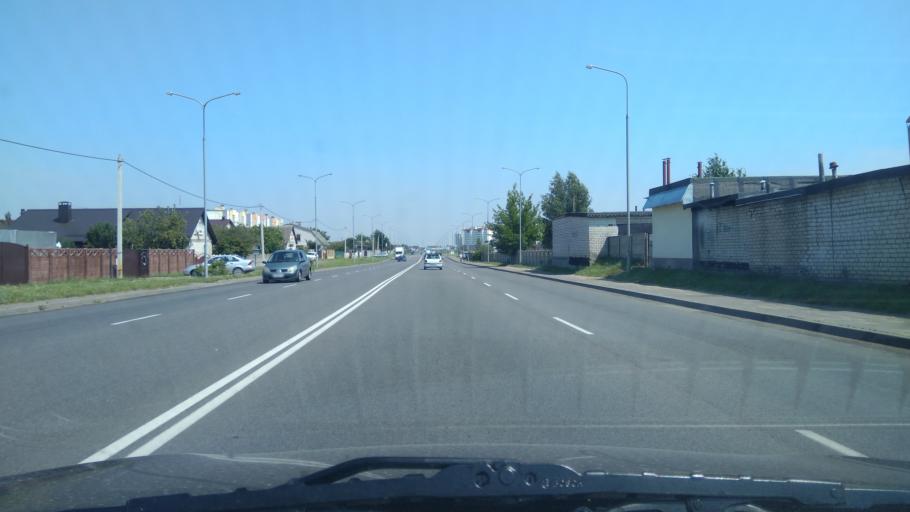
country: BY
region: Brest
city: Baranovichi
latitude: 53.1045
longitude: 25.9726
